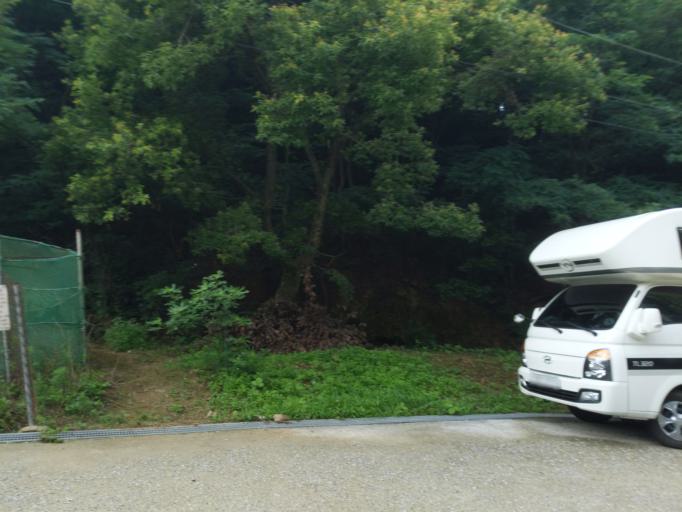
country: KR
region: Daegu
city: Hwawon
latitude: 35.7979
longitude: 128.5327
